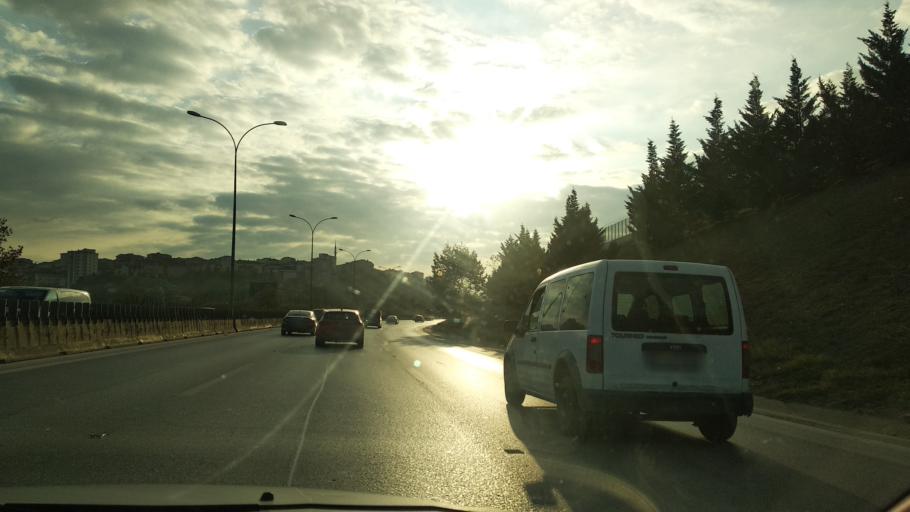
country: TR
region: Istanbul
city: Pendik
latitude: 40.8758
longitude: 29.3023
